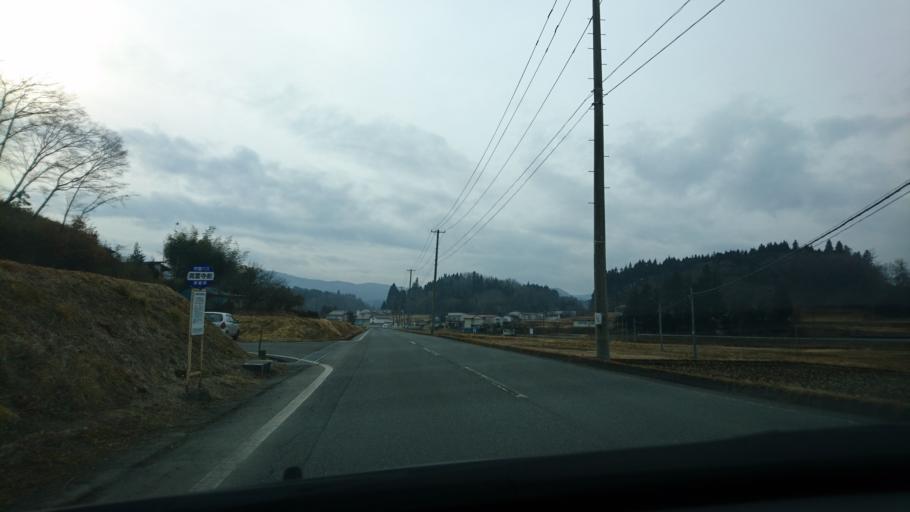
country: JP
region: Iwate
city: Ichinoseki
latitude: 38.9046
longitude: 141.3754
